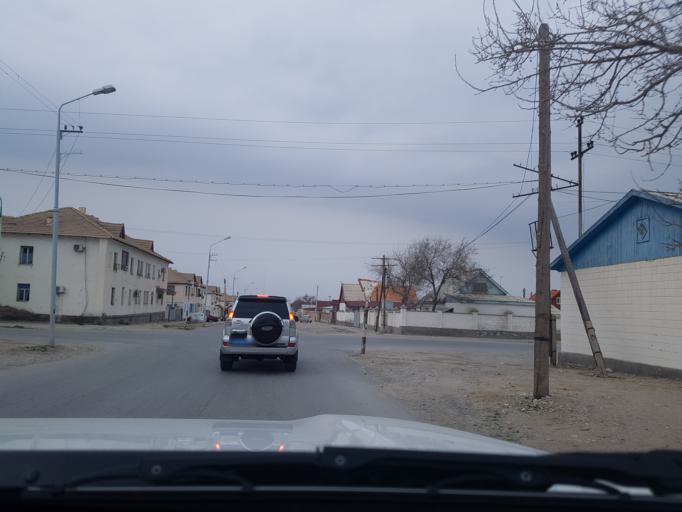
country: TM
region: Balkan
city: Balkanabat
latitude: 39.5097
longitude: 54.3773
